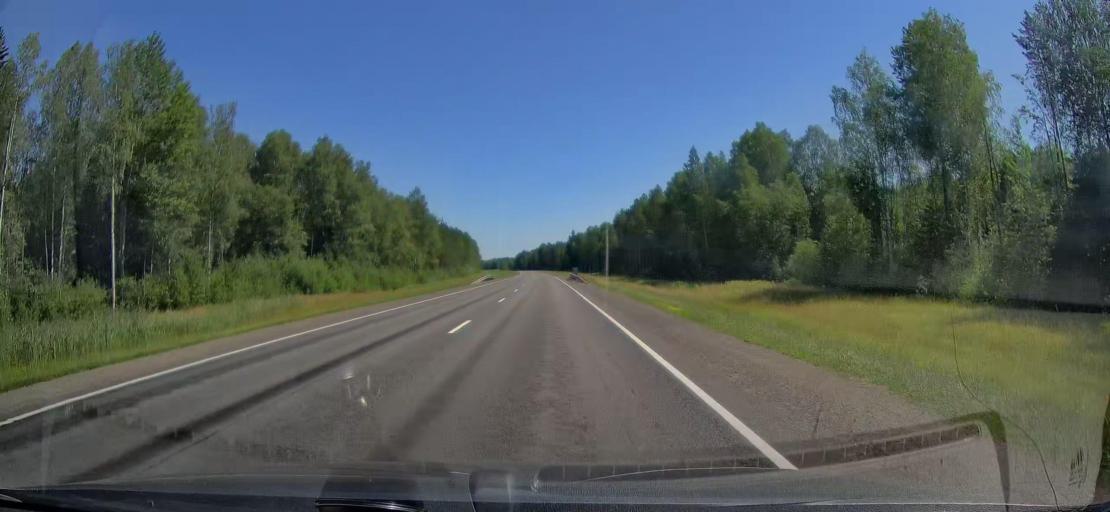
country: RU
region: Tverskaya
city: Ves'yegonsk
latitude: 58.9217
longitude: 37.2011
